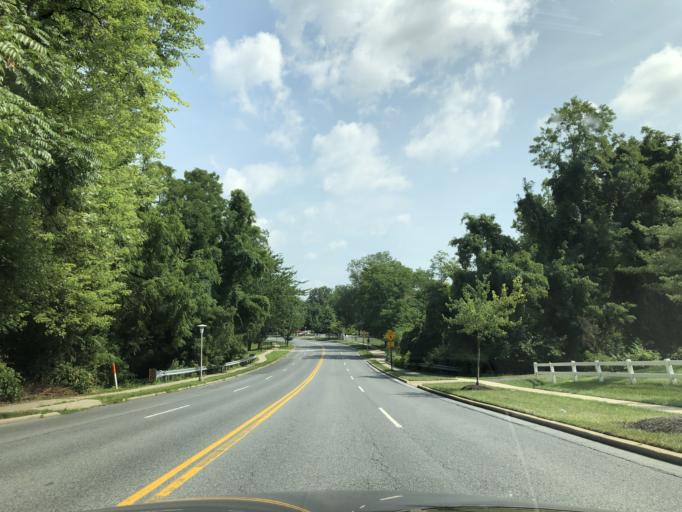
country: US
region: Maryland
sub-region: Frederick County
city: Clover Hill
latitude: 39.4229
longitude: -77.4484
